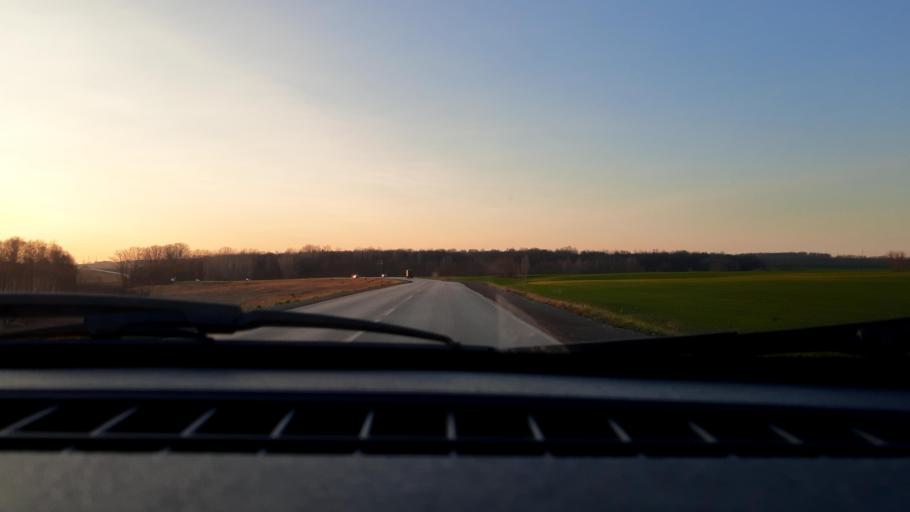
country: RU
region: Bashkortostan
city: Mikhaylovka
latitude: 54.8327
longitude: 55.9429
